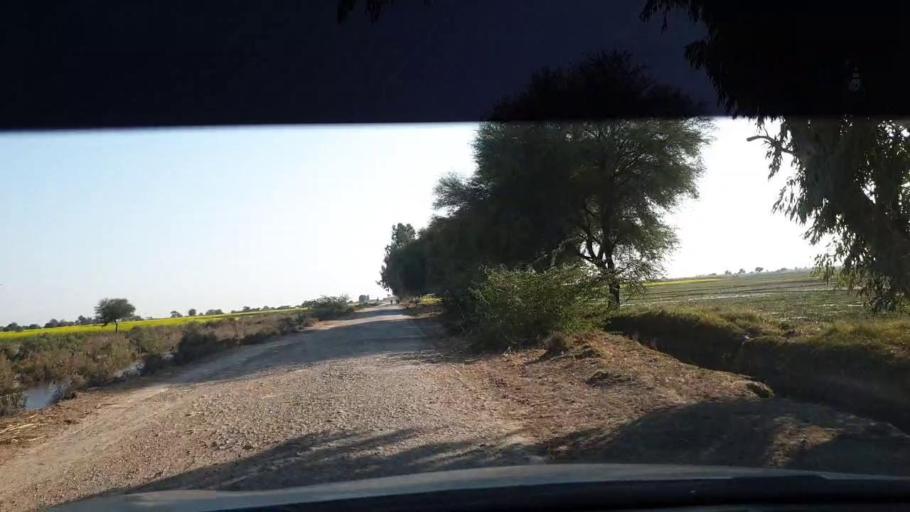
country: PK
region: Sindh
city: Berani
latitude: 25.8047
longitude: 68.9258
